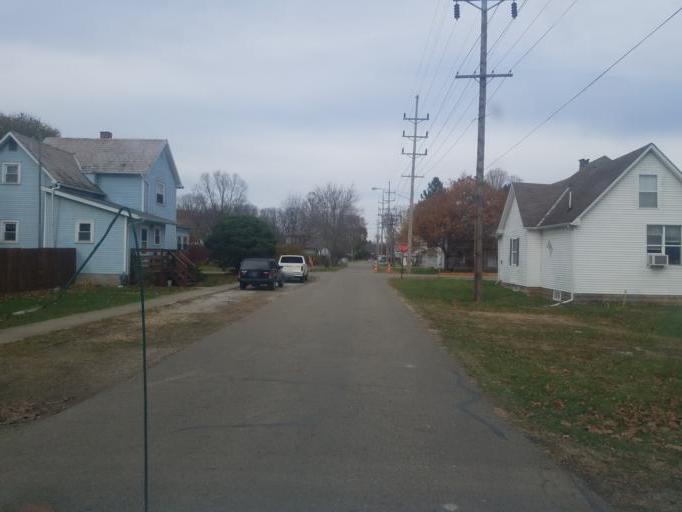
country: US
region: Ohio
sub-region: Knox County
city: Mount Vernon
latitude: 40.3975
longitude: -82.4974
